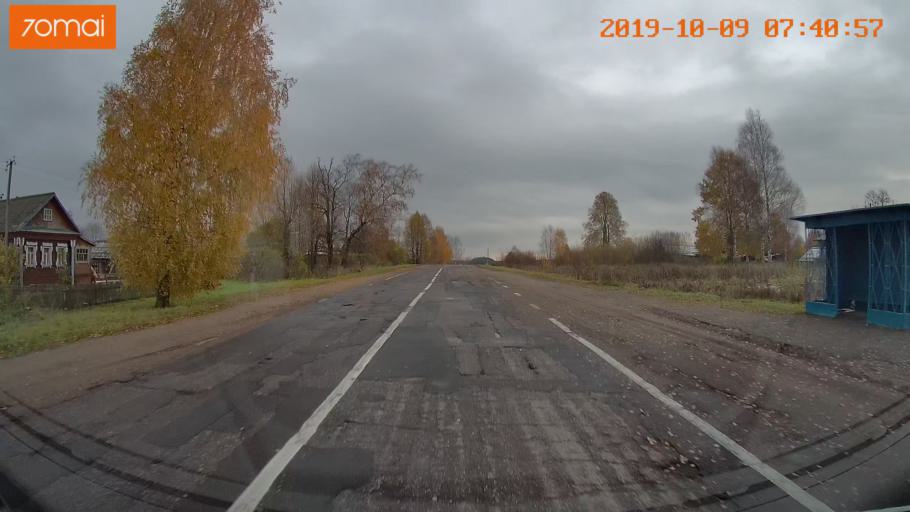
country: RU
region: Jaroslavl
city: Kukoboy
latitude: 58.6367
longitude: 39.7001
